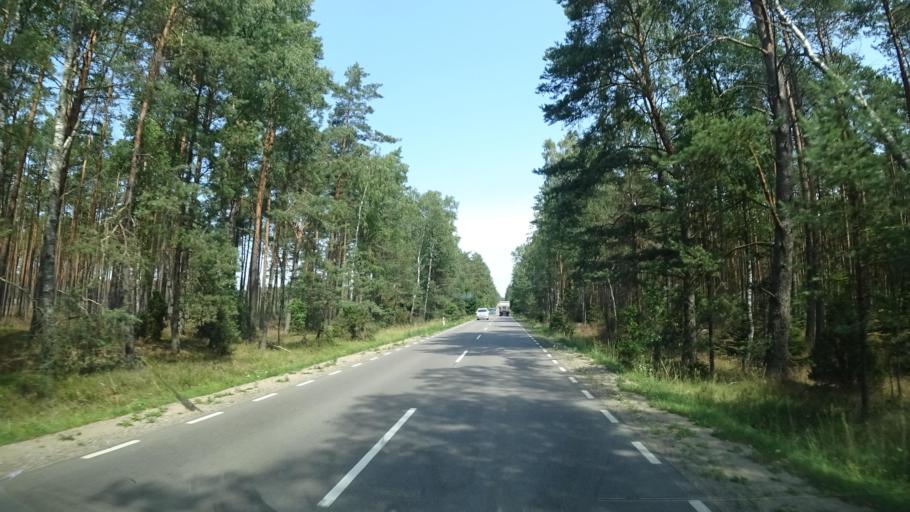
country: PL
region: Pomeranian Voivodeship
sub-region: Powiat koscierski
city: Lipusz
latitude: 54.1034
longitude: 17.8208
